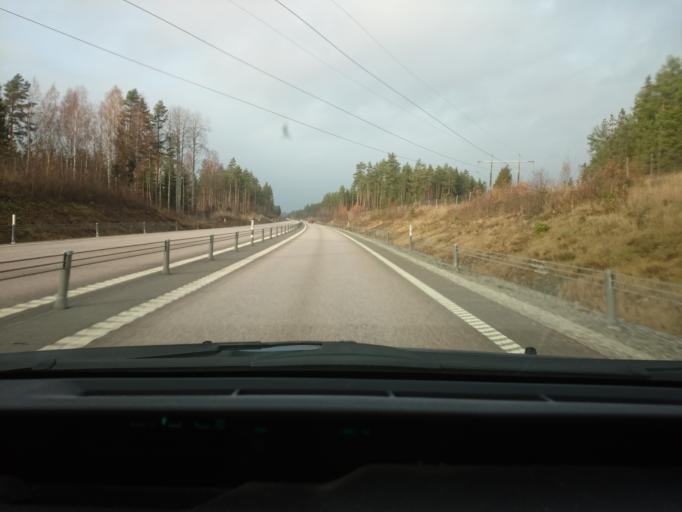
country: SE
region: Vaestmanland
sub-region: Sala Kommun
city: Sala
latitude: 59.9295
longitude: 16.5229
